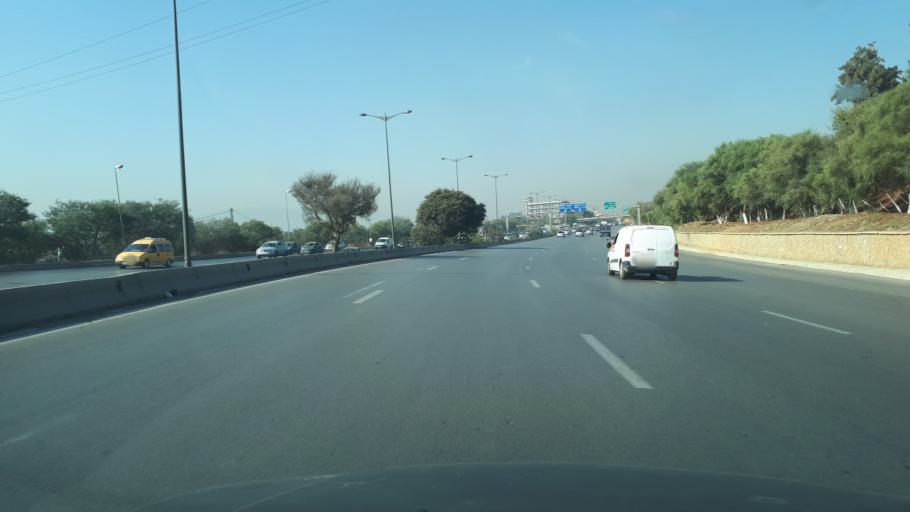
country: DZ
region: Alger
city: Birkhadem
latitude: 36.6757
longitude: 3.0563
